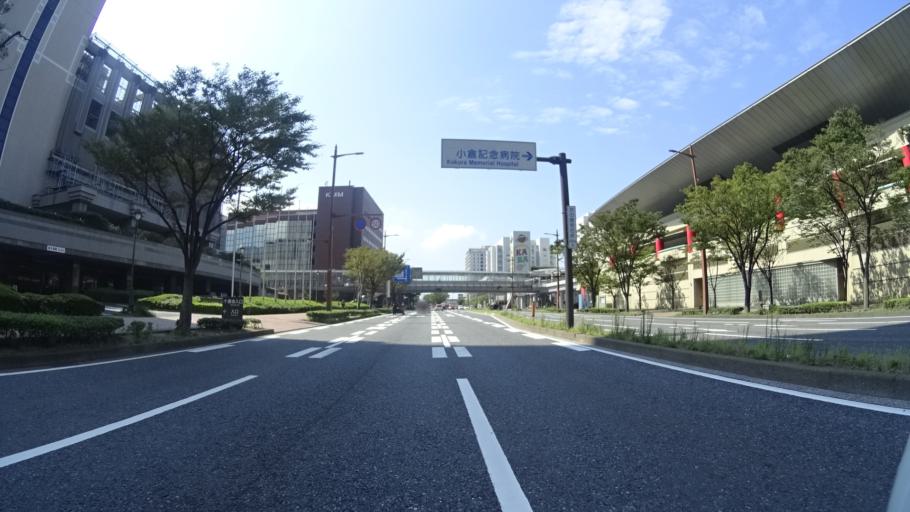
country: JP
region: Fukuoka
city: Kitakyushu
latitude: 33.8887
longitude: 130.8855
